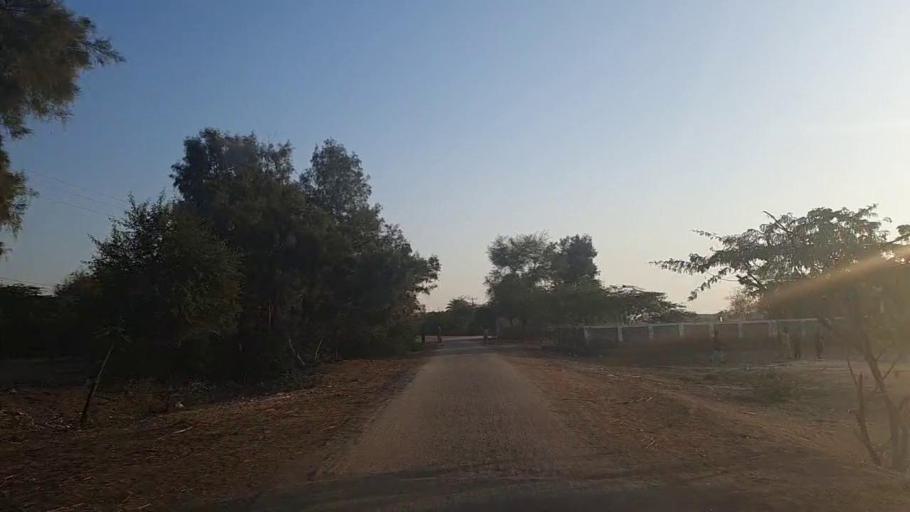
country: PK
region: Sindh
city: Jam Sahib
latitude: 26.3316
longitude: 68.6981
